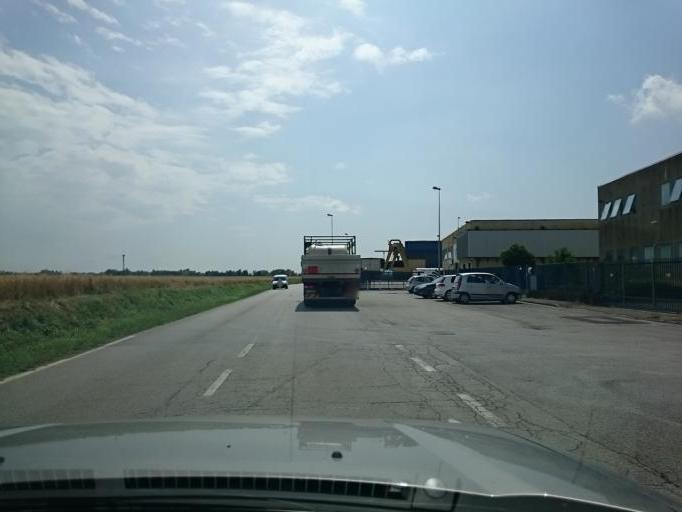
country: IT
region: Veneto
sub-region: Provincia di Padova
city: Terradura
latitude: 45.3470
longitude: 11.8326
